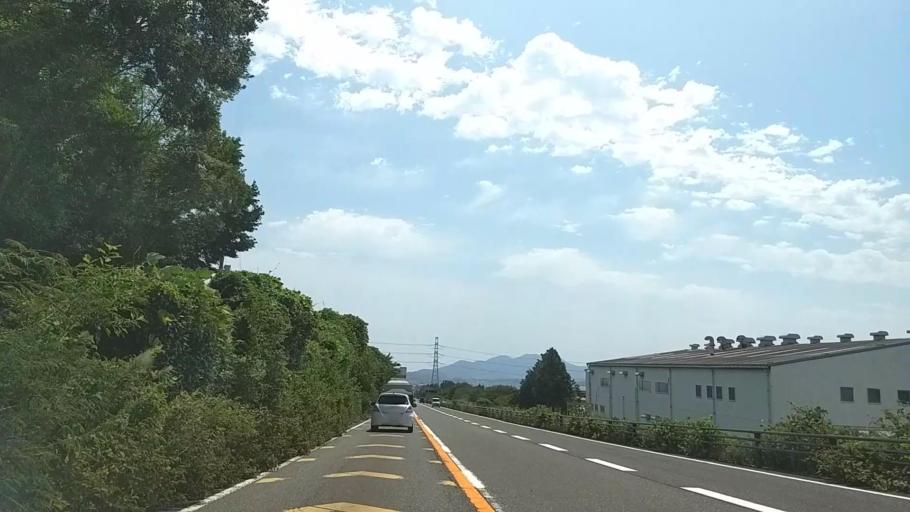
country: JP
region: Shizuoka
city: Fujinomiya
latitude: 35.2651
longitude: 138.6151
